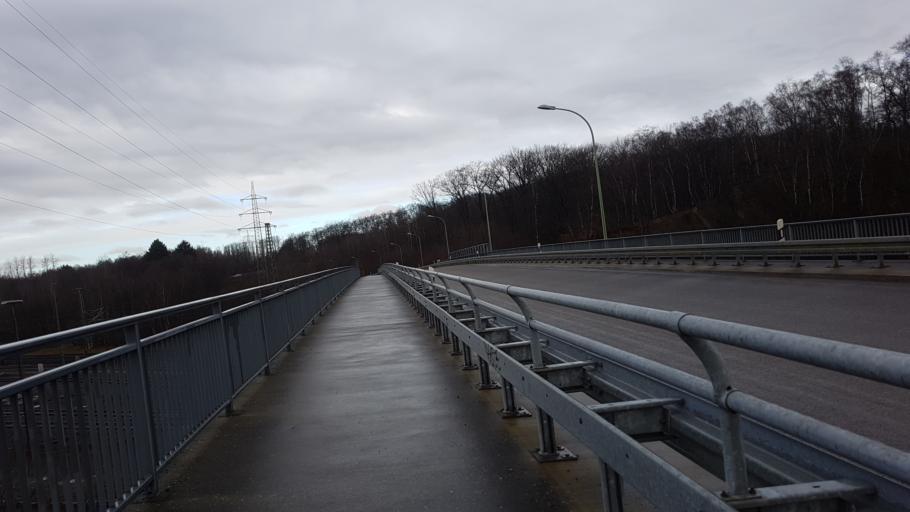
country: DE
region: North Rhine-Westphalia
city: Stolberg
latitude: 50.7929
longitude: 6.2144
